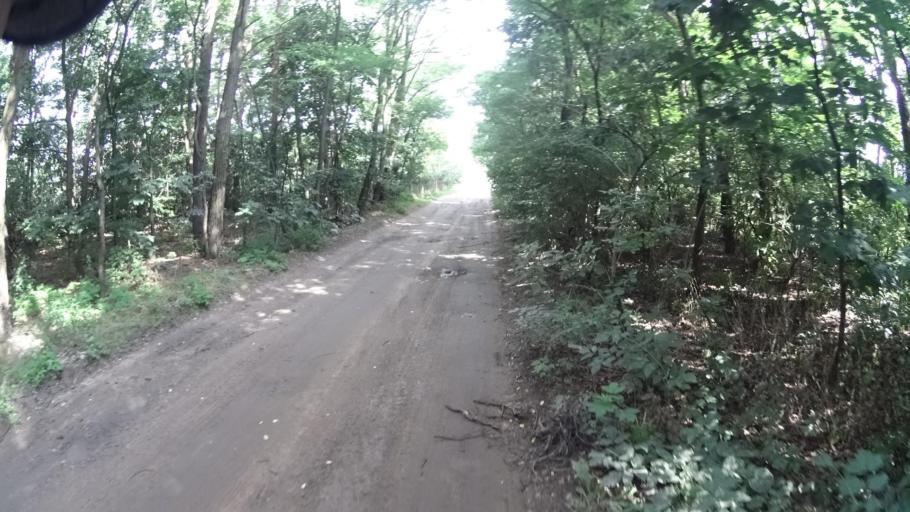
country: PL
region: Masovian Voivodeship
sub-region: Powiat piaseczynski
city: Tarczyn
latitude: 51.9674
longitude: 20.8543
